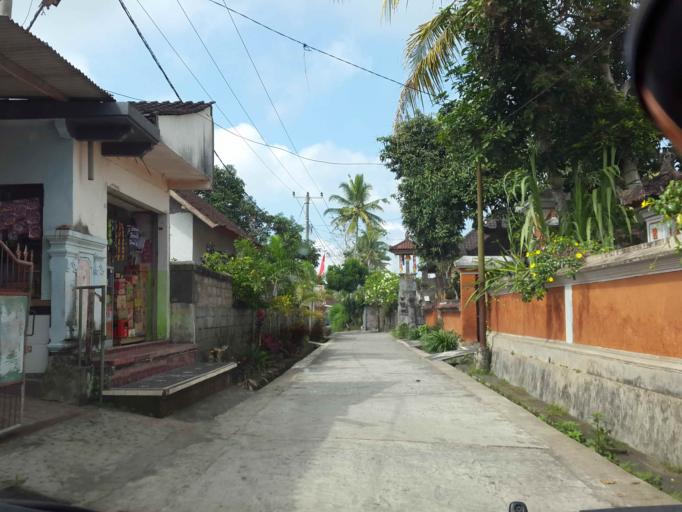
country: ID
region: Bali
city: Bangli
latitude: -8.4652
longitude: 115.3829
